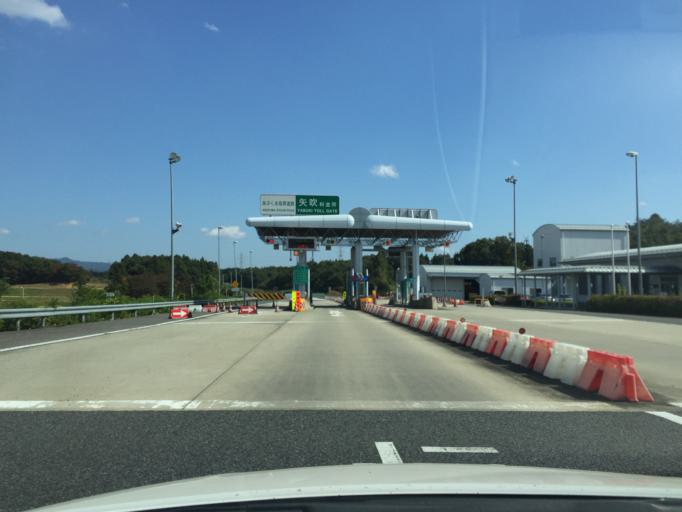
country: JP
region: Fukushima
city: Sukagawa
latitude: 37.2004
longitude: 140.3649
